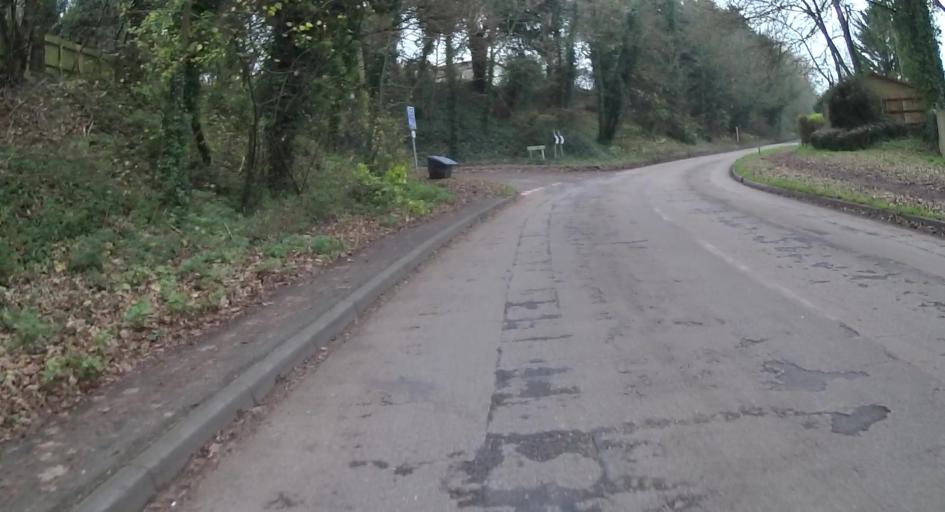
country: GB
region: England
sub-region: Hampshire
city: Kings Worthy
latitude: 51.0871
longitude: -1.3094
